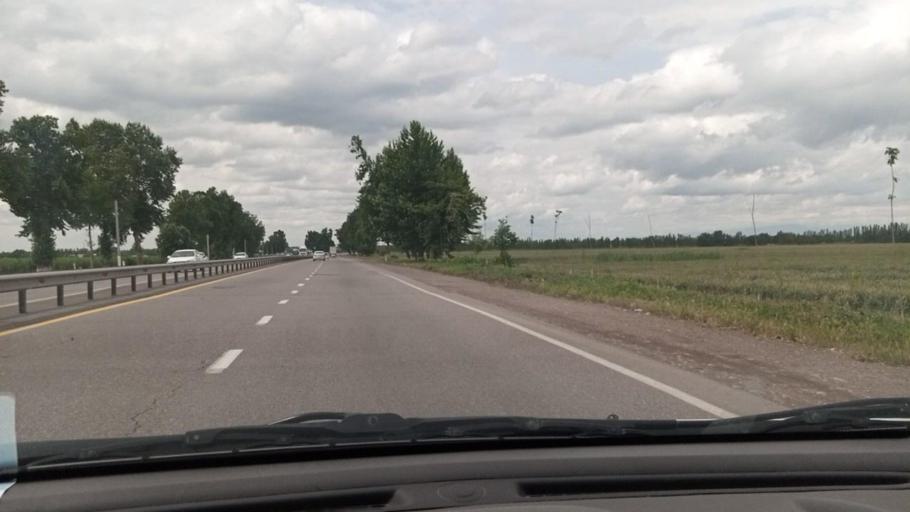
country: UZ
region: Toshkent Shahri
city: Bektemir
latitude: 41.1400
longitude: 69.4334
